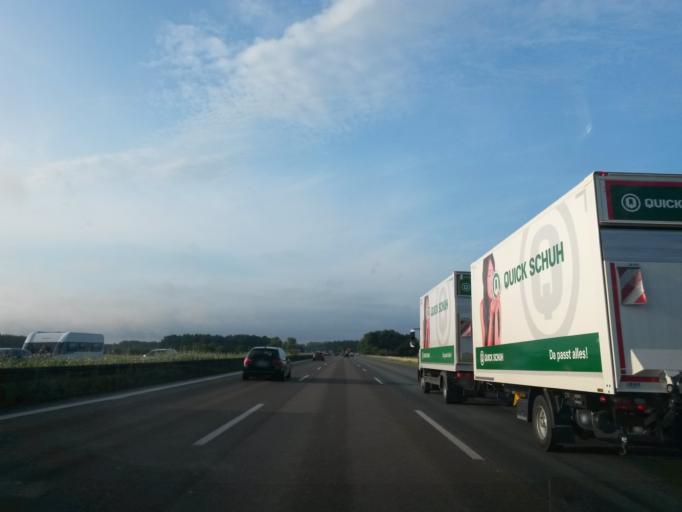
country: DE
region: Bavaria
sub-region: Upper Bavaria
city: Manching
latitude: 48.7001
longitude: 11.4892
